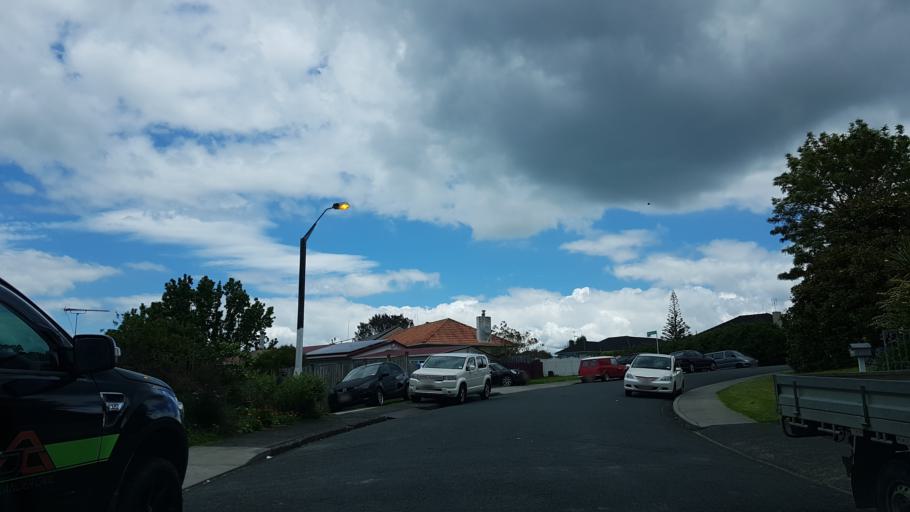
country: NZ
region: Auckland
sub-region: Auckland
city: North Shore
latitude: -36.7932
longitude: 174.6961
